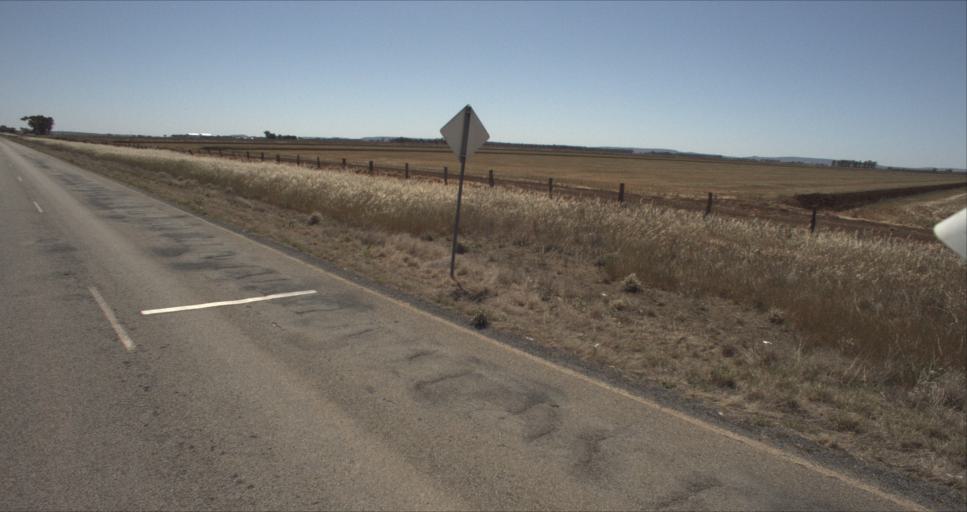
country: AU
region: New South Wales
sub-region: Leeton
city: Leeton
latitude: -34.5167
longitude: 146.2840
